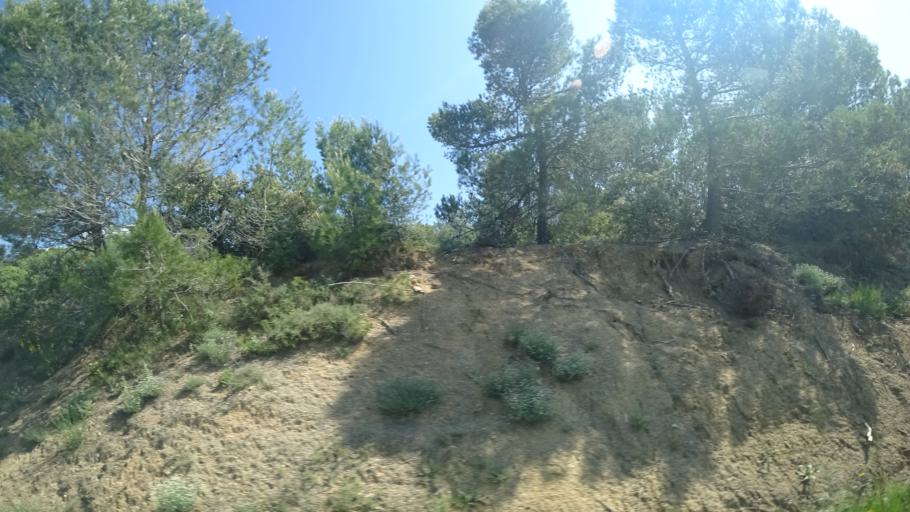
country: FR
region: Languedoc-Roussillon
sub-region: Departement de l'Herault
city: Olonzac
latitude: 43.3310
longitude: 2.7384
